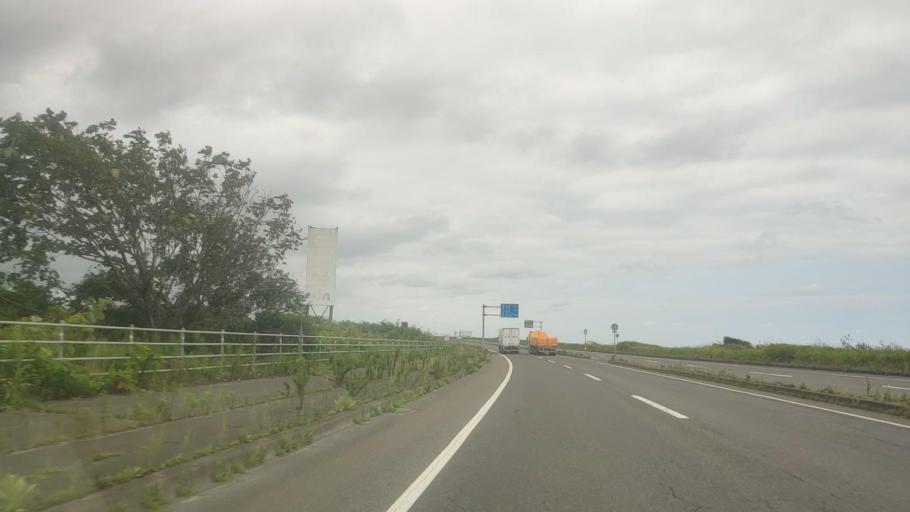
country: JP
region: Hokkaido
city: Shiraoi
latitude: 42.5385
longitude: 141.3375
